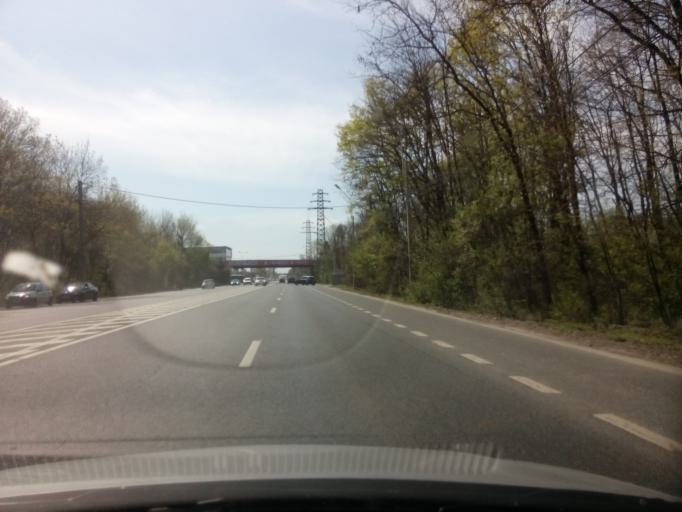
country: RO
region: Ilfov
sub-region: Comuna Corbeanca
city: Corbeanca
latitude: 44.5857
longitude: 26.0705
